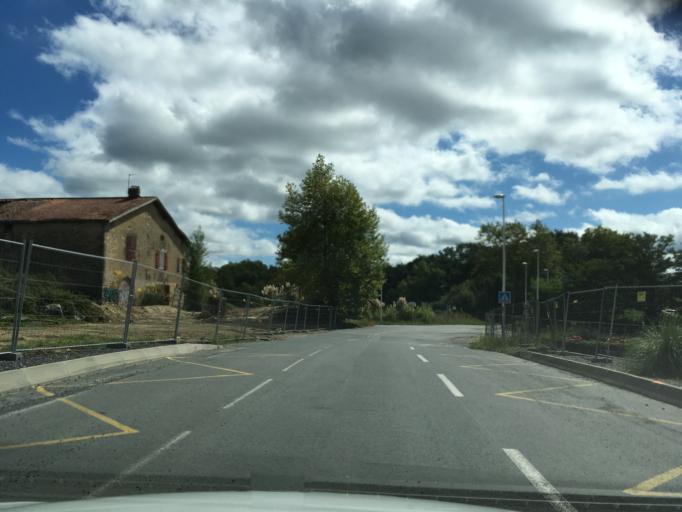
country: FR
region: Aquitaine
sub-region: Departement des Pyrenees-Atlantiques
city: Boucau
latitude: 43.5067
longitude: -1.4313
